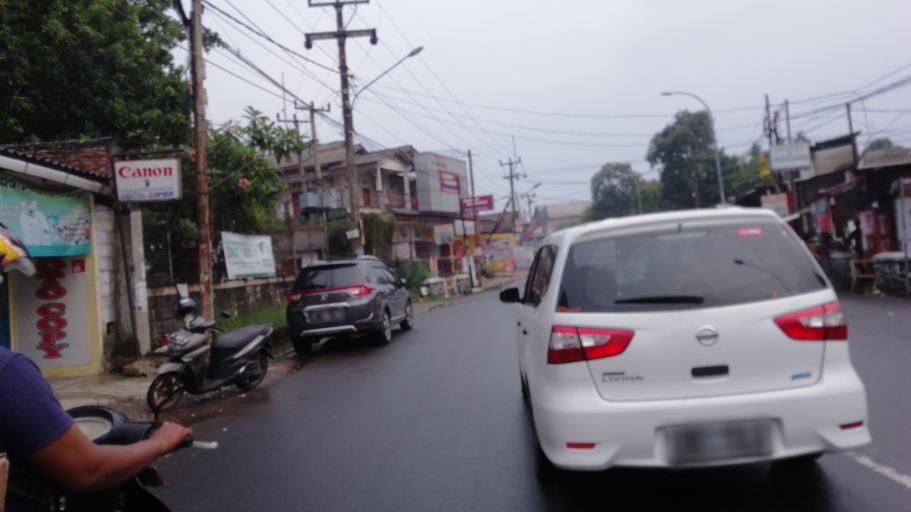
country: ID
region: West Java
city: Bogor
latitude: -6.5450
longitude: 106.8059
